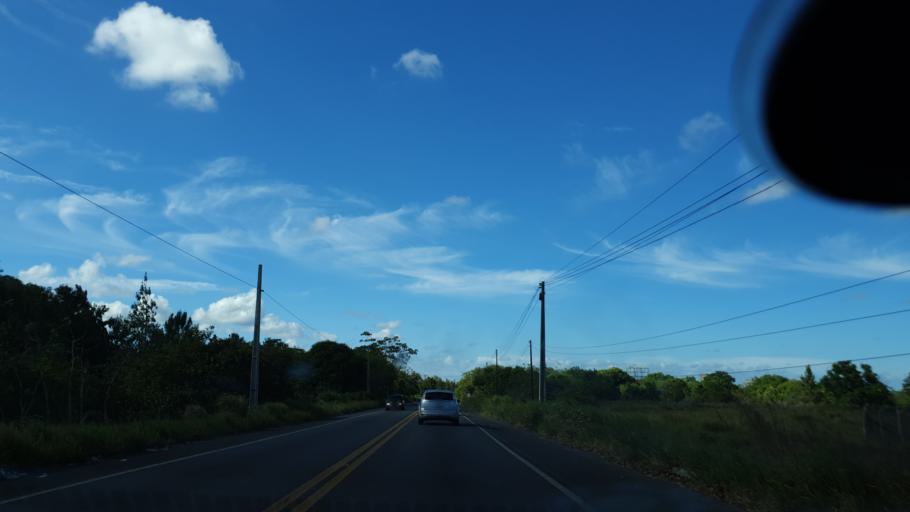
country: BR
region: Bahia
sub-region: Camacari
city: Camacari
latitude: -12.6639
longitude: -38.3014
